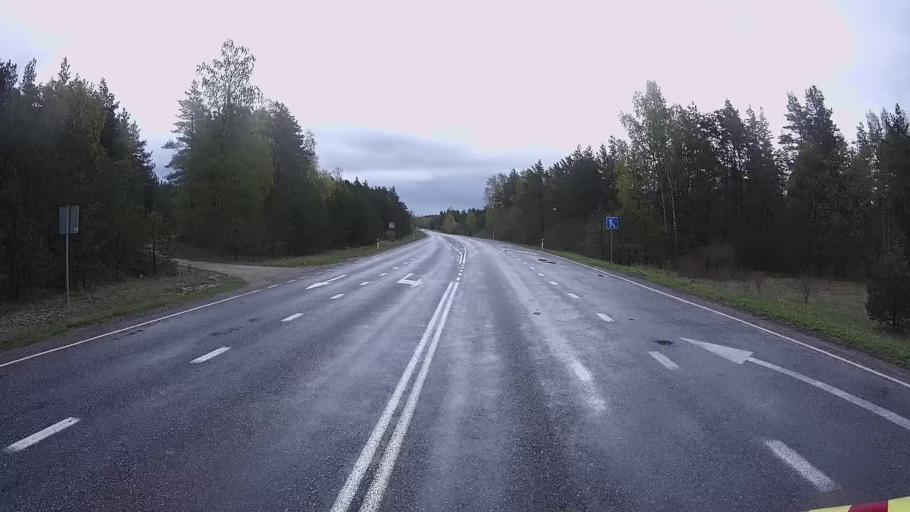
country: EE
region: Hiiumaa
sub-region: Kaerdla linn
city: Kardla
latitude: 58.8699
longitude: 22.9660
